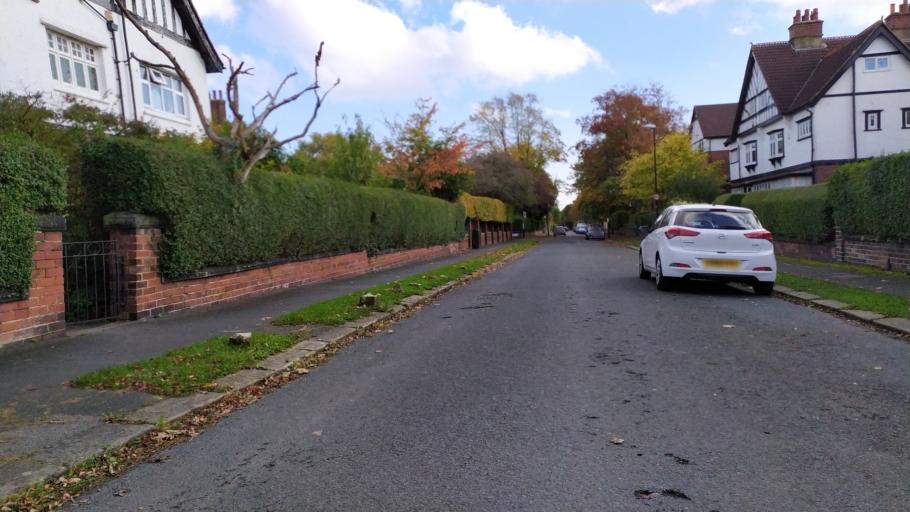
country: GB
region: England
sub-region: City and Borough of Leeds
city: Horsforth
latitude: 53.8336
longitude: -1.5982
